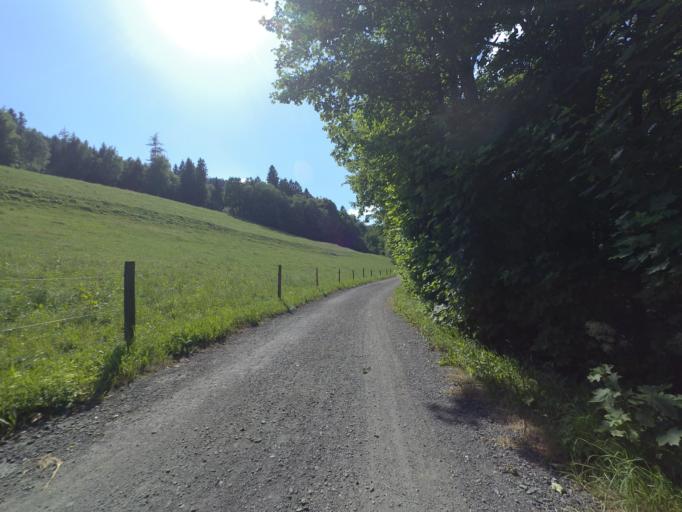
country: AT
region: Carinthia
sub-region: Politischer Bezirk Spittal an der Drau
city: Millstatt
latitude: 46.7725
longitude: 13.6084
